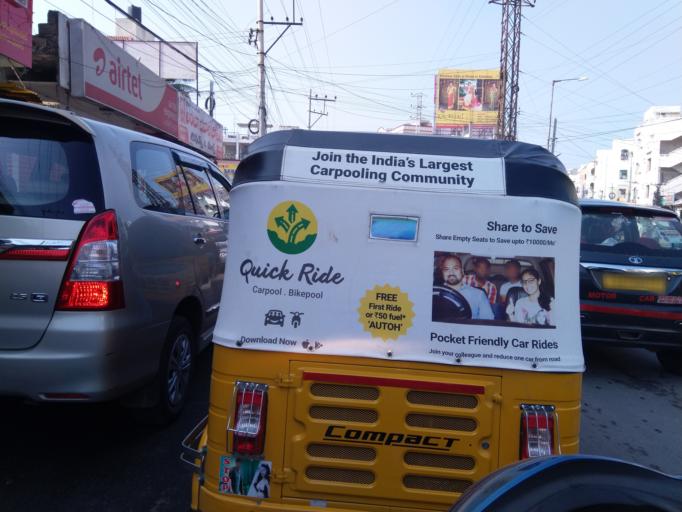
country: IN
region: Telangana
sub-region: Rangareddi
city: Kukatpalli
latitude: 17.4967
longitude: 78.4066
